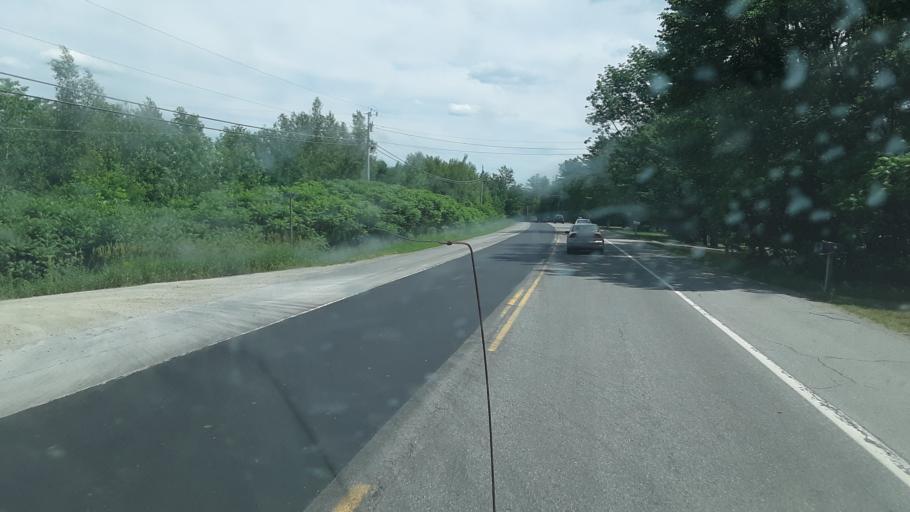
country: US
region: Maine
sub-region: Somerset County
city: Fairfield
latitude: 44.6396
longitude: -69.6896
